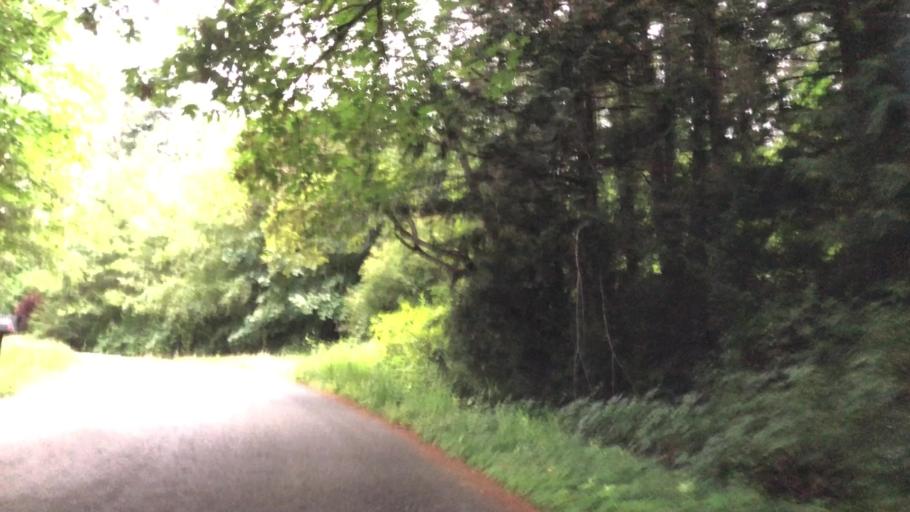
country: US
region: Washington
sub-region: King County
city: Cottage Lake
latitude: 47.7233
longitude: -122.0875
